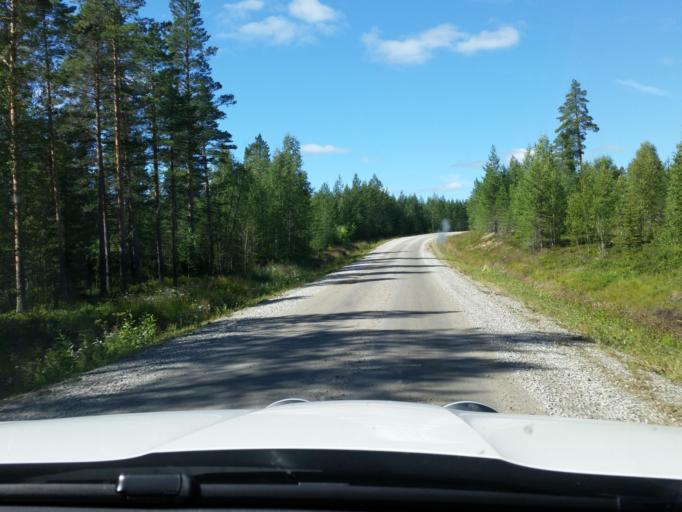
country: SE
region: Vaesterbotten
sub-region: Skelleftea Kommun
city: Backa
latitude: 65.1933
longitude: 21.0310
